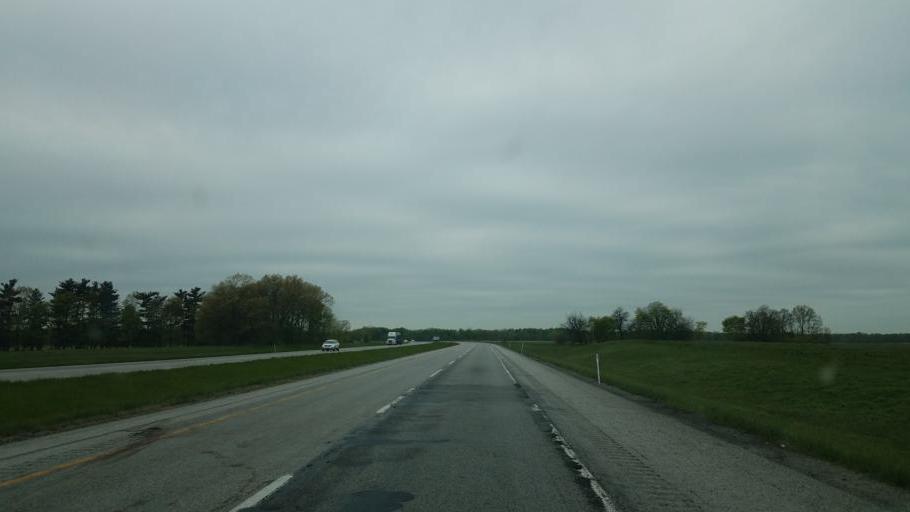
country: US
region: Michigan
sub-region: Saint Joseph County
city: White Pigeon
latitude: 41.7518
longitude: -85.5659
